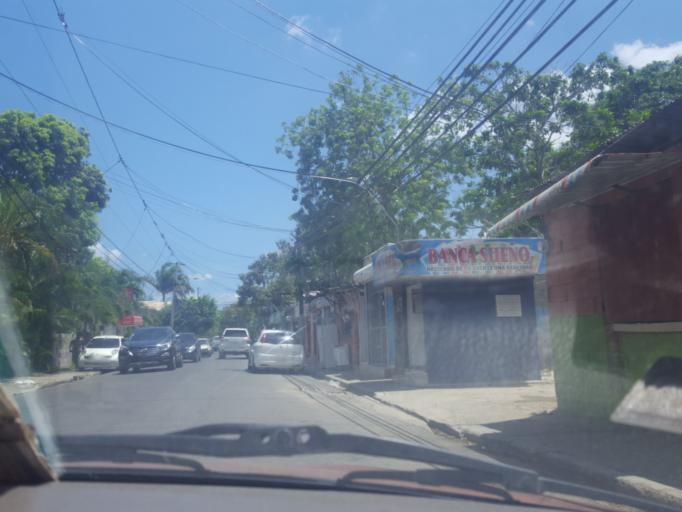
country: DO
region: Santiago
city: Santiago de los Caballeros
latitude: 19.4716
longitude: -70.6641
